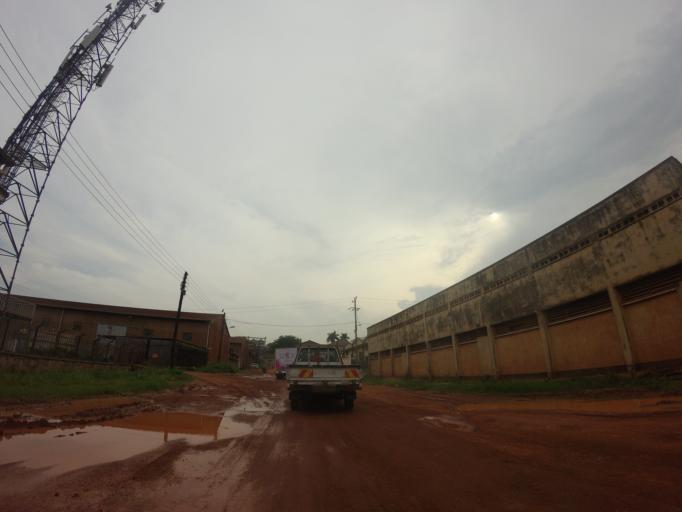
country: UG
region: Central Region
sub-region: Wakiso District
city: Kireka
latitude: 0.3382
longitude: 32.6219
